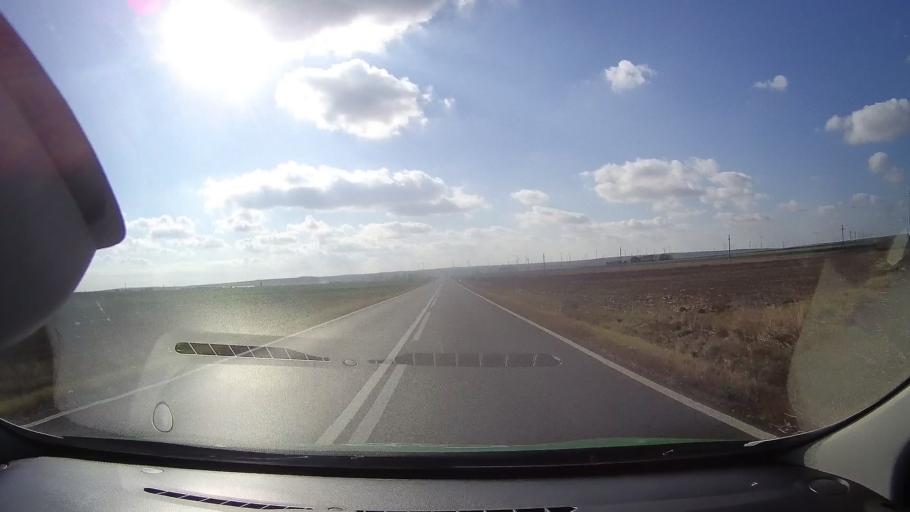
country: RO
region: Constanta
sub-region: Comuna Mihai Viteazu
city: Mihai Viteazu
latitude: 44.6607
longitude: 28.6761
